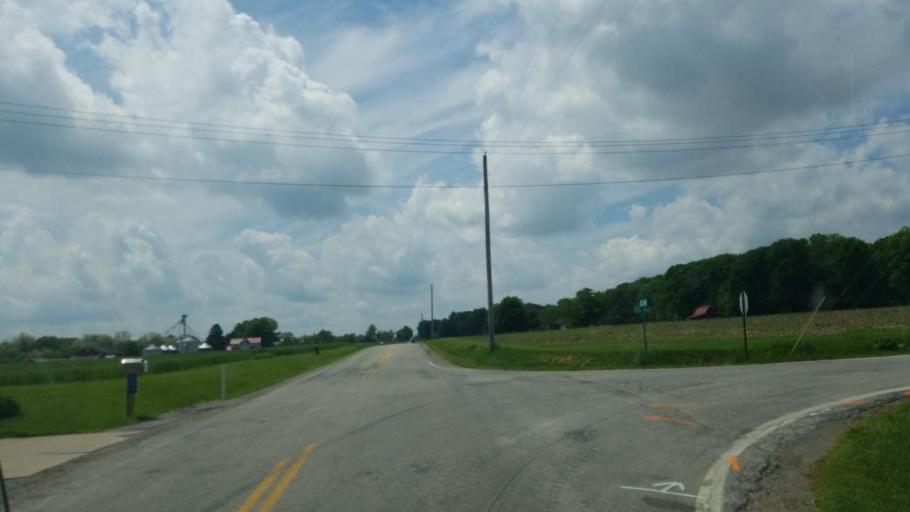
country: US
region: Ohio
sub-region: Ashland County
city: Ashland
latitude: 40.8059
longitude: -82.3151
